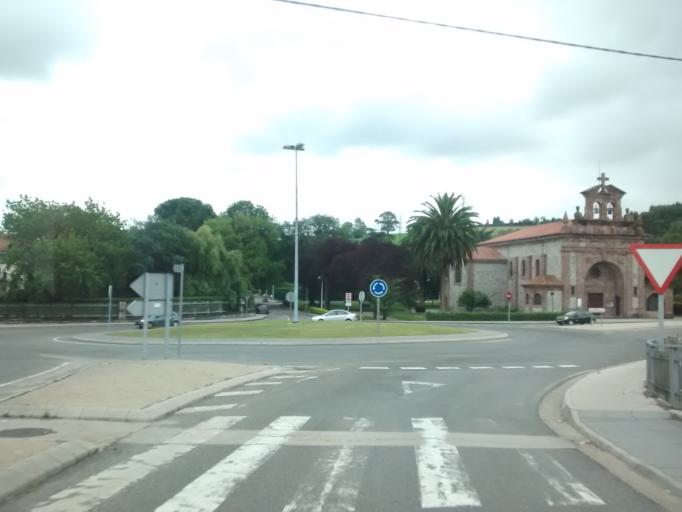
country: ES
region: Cantabria
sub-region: Provincia de Cantabria
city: Torrelavega
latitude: 43.3733
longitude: -4.0418
